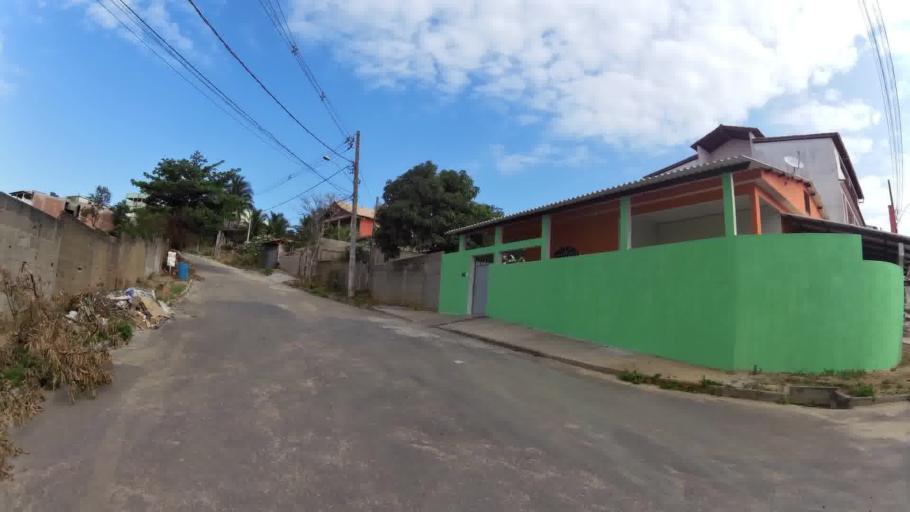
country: BR
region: Espirito Santo
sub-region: Itapemirim
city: Itapemirim
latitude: -21.0115
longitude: -40.8291
